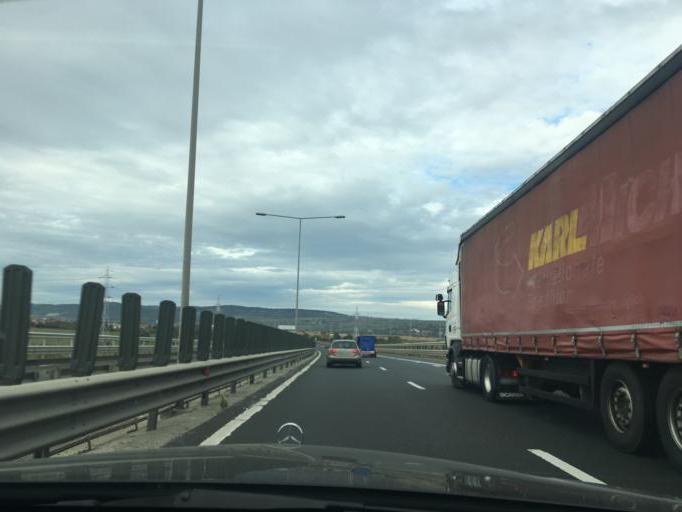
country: RO
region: Sibiu
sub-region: Comuna Selimbar
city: Selimbar
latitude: 45.7544
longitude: 24.2051
